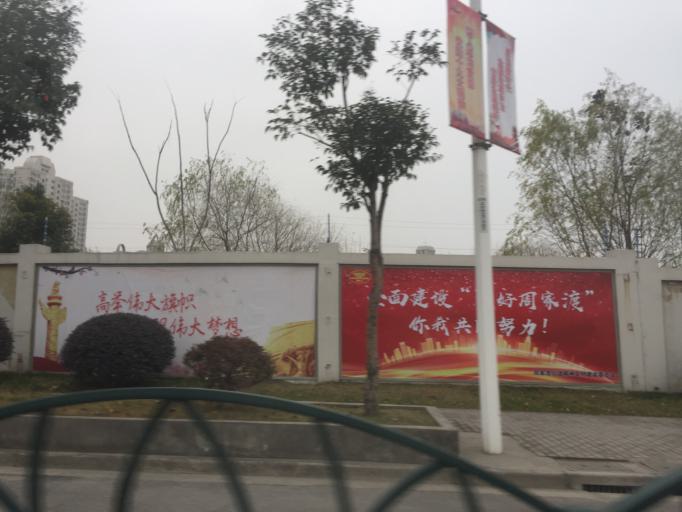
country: CN
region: Shanghai Shi
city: Luwan
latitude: 31.1872
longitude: 121.4975
